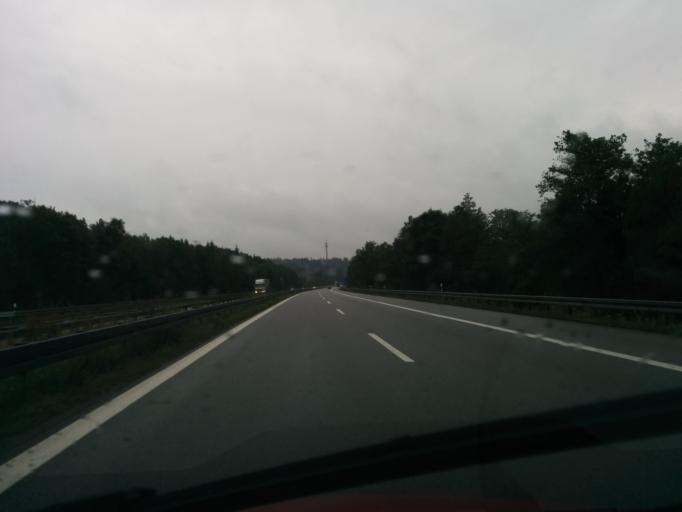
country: DE
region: Bavaria
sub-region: Lower Bavaria
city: Passau
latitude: 48.5491
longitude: 13.3965
